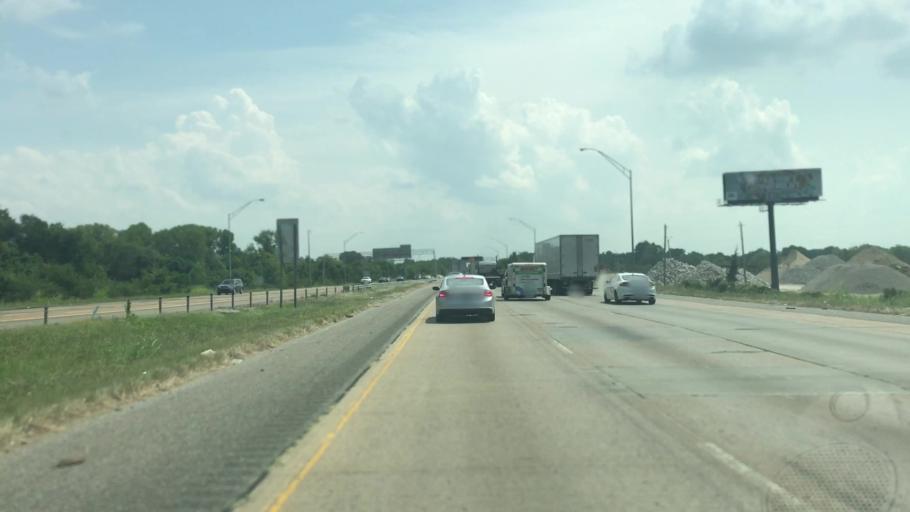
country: US
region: Tennessee
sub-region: Shelby County
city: Memphis
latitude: 35.1845
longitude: -90.0179
